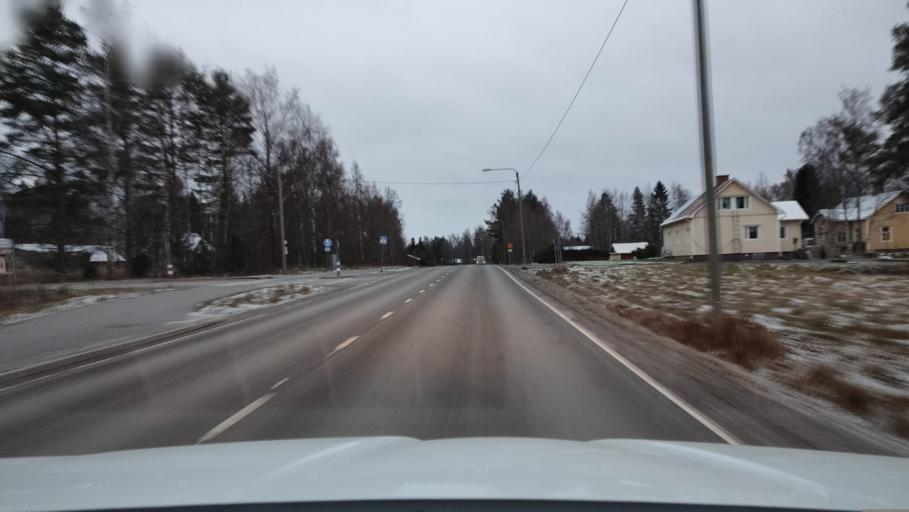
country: FI
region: Ostrobothnia
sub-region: Vaasa
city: Replot
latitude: 63.2258
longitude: 21.4111
